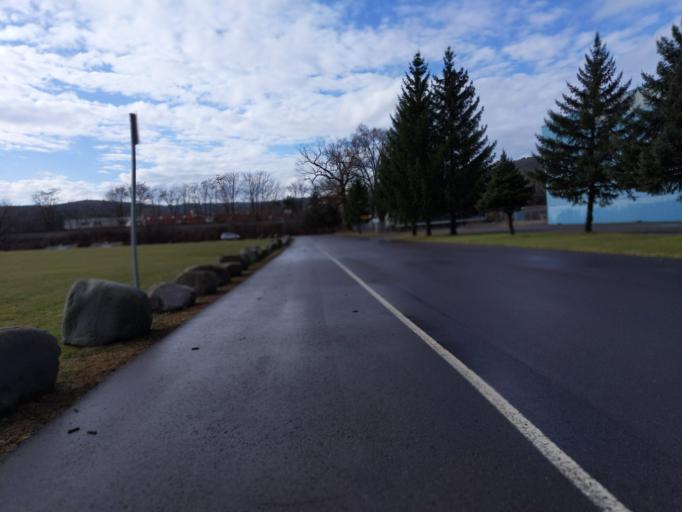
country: US
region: New York
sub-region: Chemung County
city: Elmira Heights
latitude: 42.1174
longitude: -76.8194
